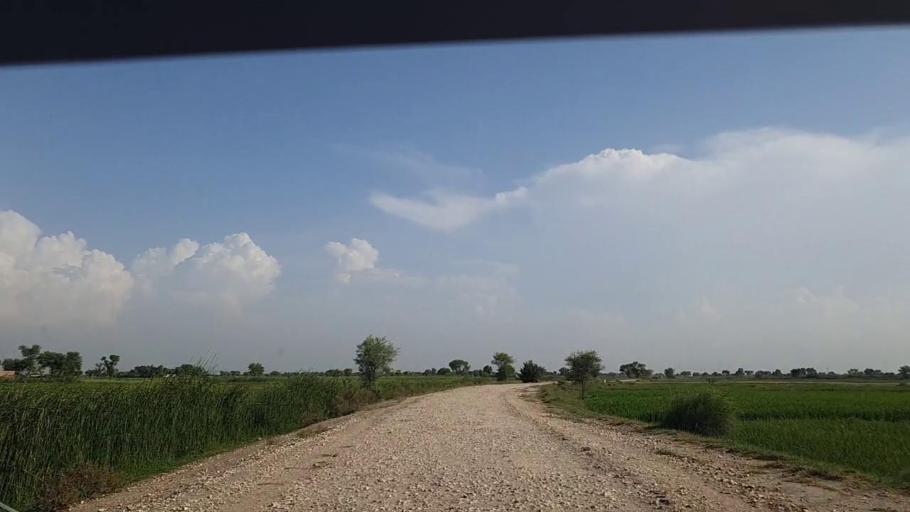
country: PK
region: Sindh
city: Khanpur
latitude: 27.8498
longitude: 69.3777
